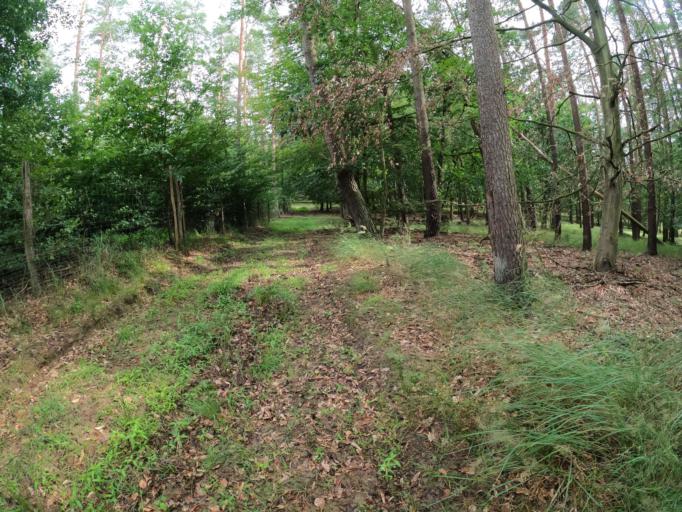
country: DE
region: Brandenburg
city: Angermunde
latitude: 53.0302
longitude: 13.9189
